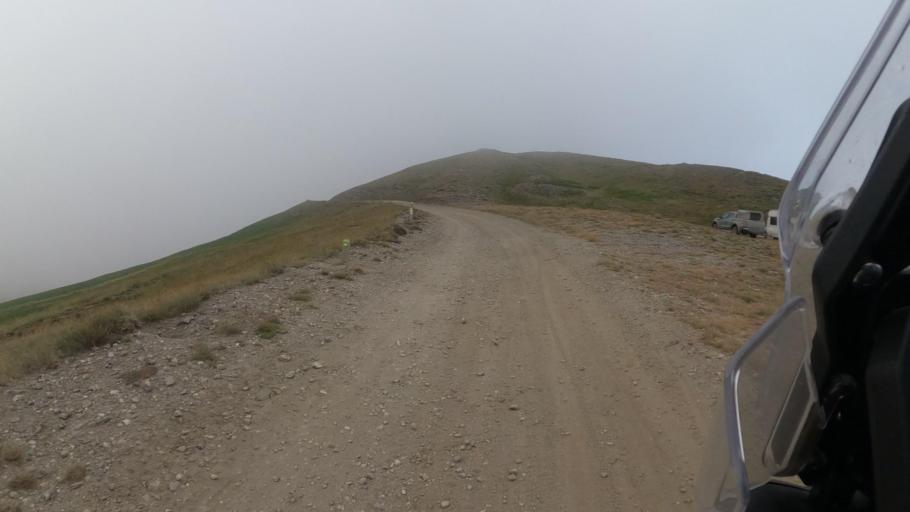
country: IT
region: Piedmont
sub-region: Provincia di Torino
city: Exilles
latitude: 45.0594
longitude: 6.9363
